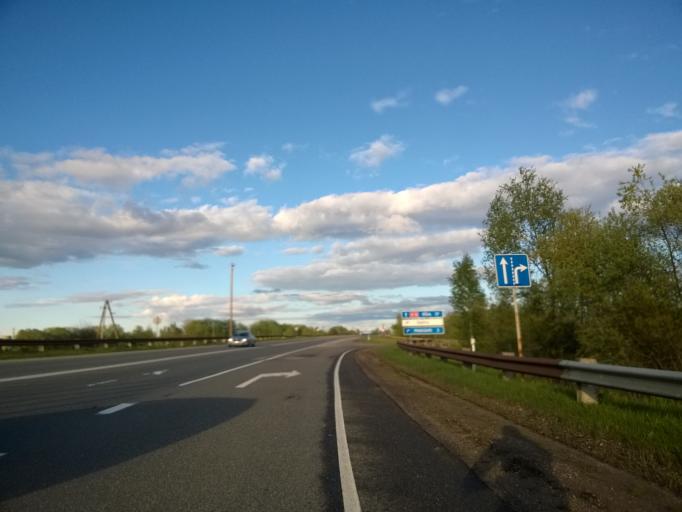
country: LV
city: Tireli
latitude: 56.9324
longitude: 23.5992
